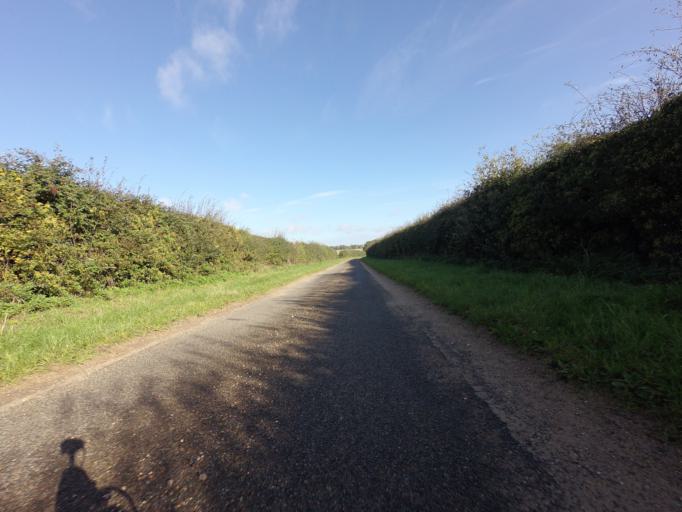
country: GB
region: England
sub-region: Norfolk
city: Fakenham
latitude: 52.8347
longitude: 0.6756
